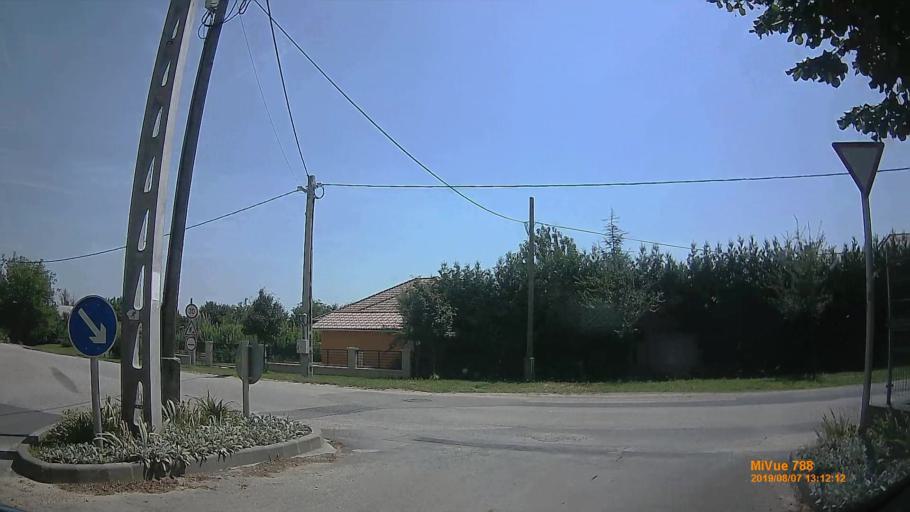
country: HU
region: Zala
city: Cserszegtomaj
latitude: 46.8055
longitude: 17.2236
